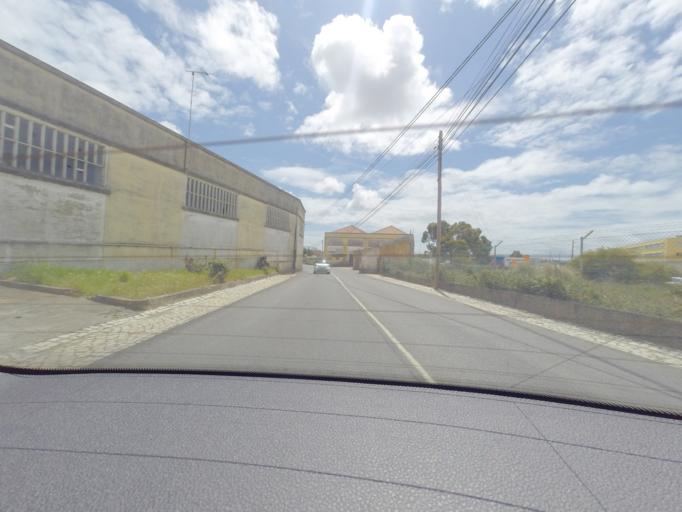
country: PT
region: Lisbon
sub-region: Cascais
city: Alcabideche
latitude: 38.7404
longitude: -9.3931
